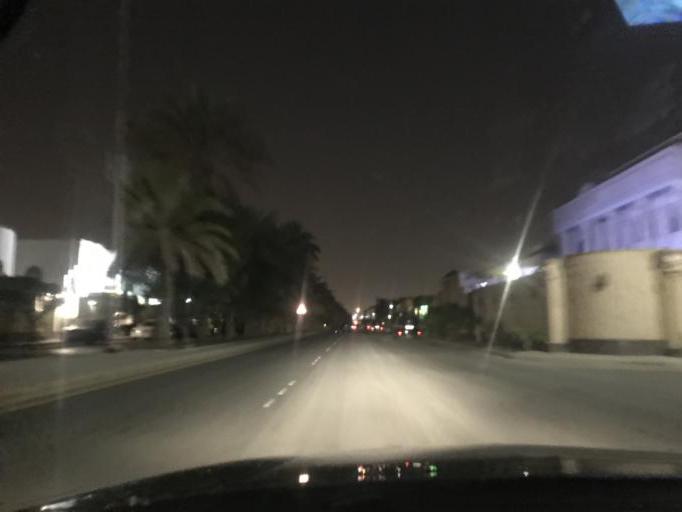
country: SA
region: Ar Riyad
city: Riyadh
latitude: 24.7125
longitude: 46.7786
